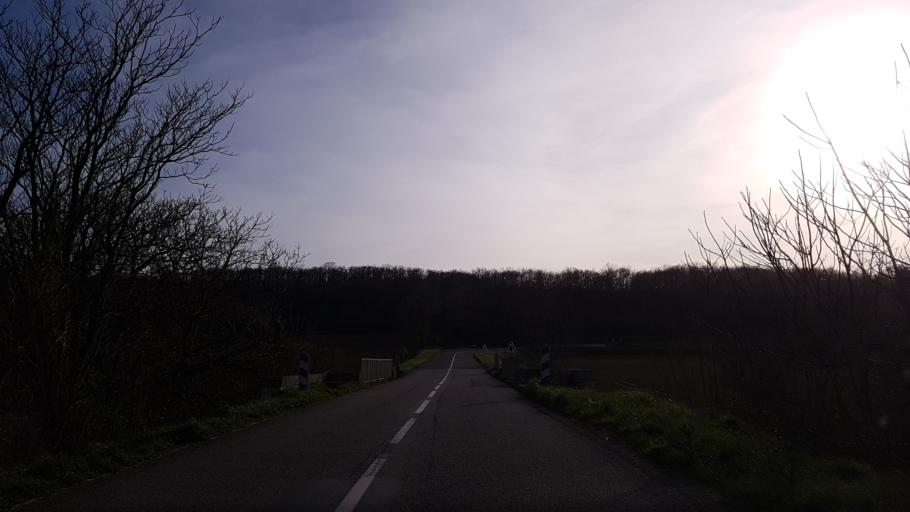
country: FR
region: Languedoc-Roussillon
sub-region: Departement de l'Aude
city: Villeneuve-la-Comptal
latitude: 43.2420
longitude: 1.9215
